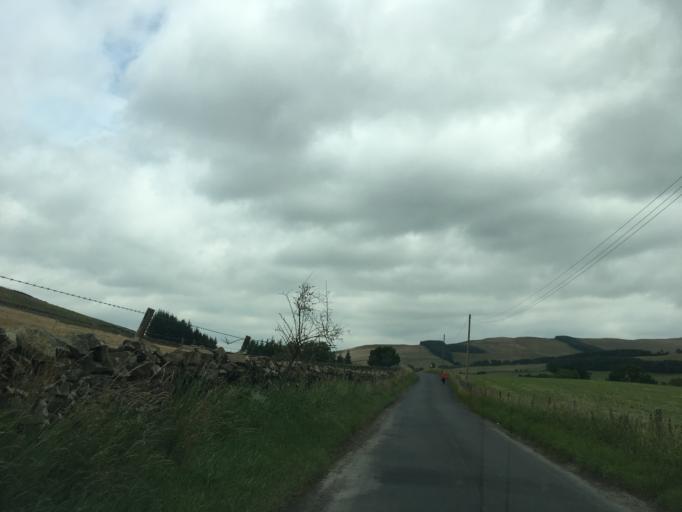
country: GB
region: Scotland
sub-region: The Scottish Borders
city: Peebles
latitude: 55.6633
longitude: -3.2016
